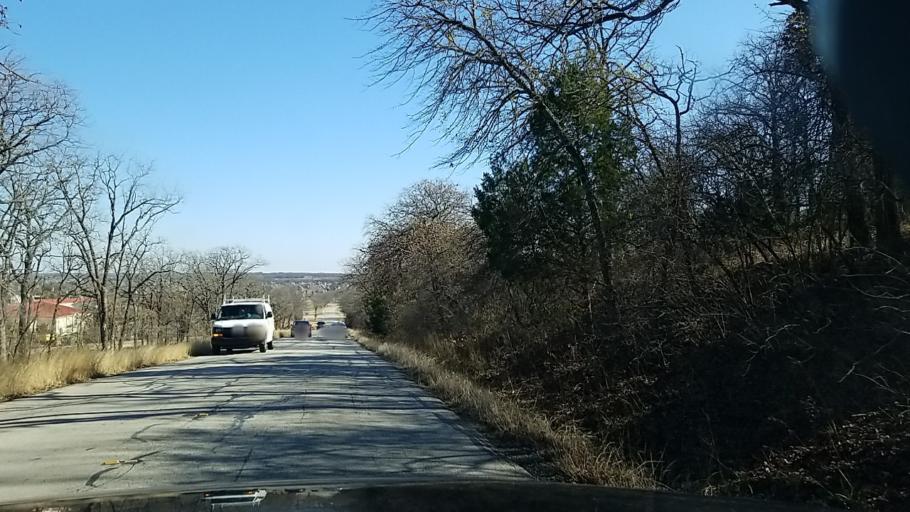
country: US
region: Texas
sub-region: Denton County
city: Argyle
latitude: 33.1309
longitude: -97.2008
